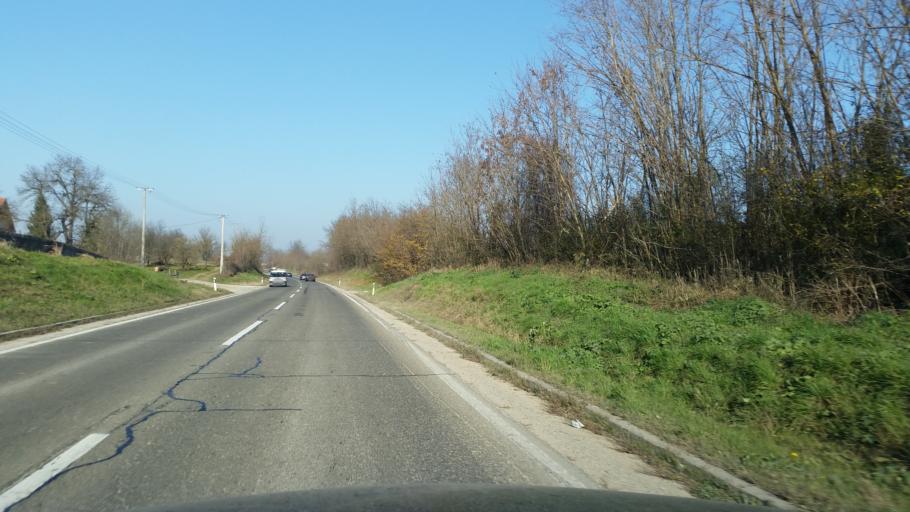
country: RS
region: Central Serbia
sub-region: Kolubarski Okrug
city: Ljig
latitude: 44.2551
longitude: 20.2863
